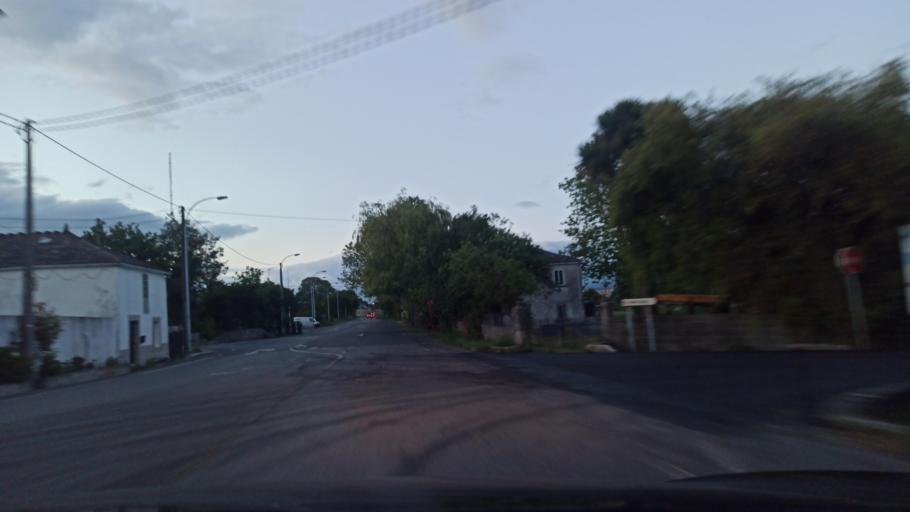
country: ES
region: Galicia
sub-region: Provincia de Lugo
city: Lugo
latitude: 42.9882
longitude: -7.5797
